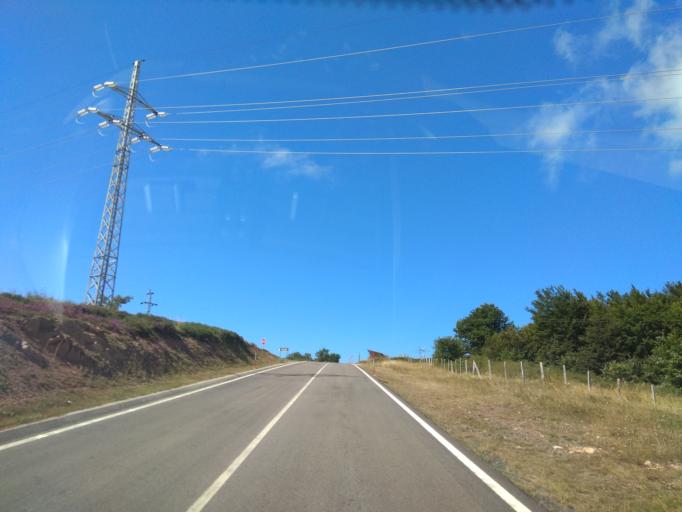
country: ES
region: Cantabria
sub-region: Provincia de Cantabria
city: Villaescusa
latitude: 42.9428
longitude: -4.1525
